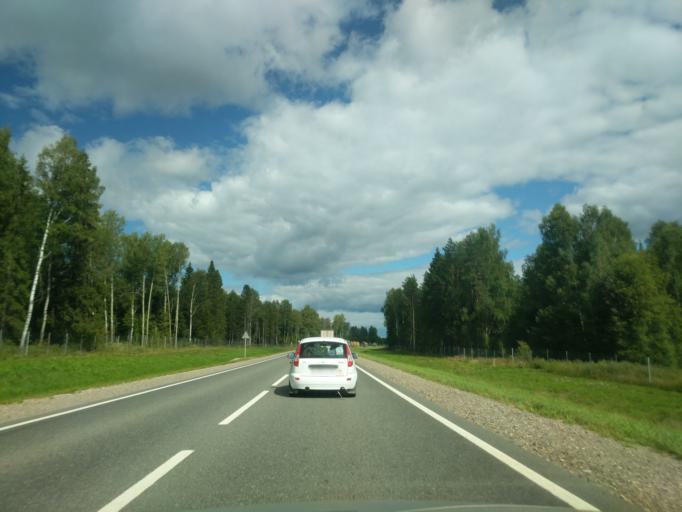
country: RU
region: Kostroma
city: Oktyabr'skiy
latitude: 57.8007
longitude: 41.2712
